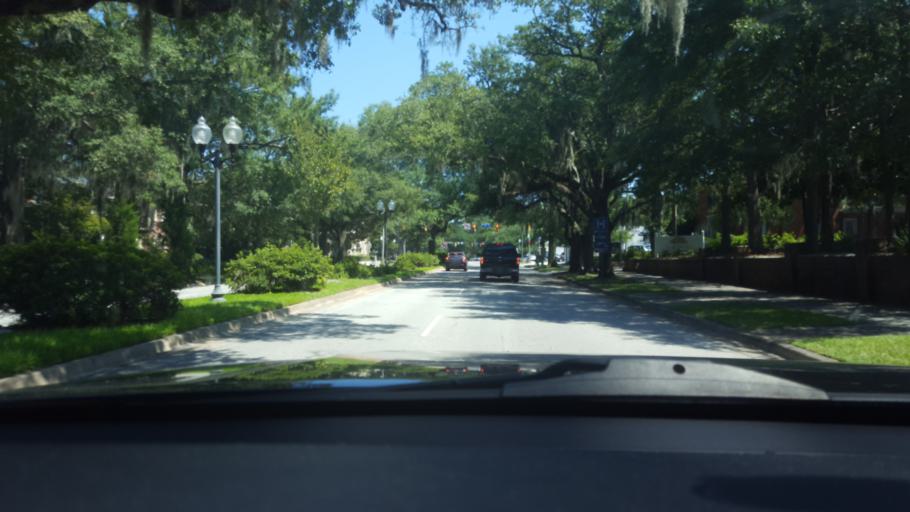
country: US
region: North Carolina
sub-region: New Hanover County
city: Wilmington
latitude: 34.2368
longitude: -77.9300
